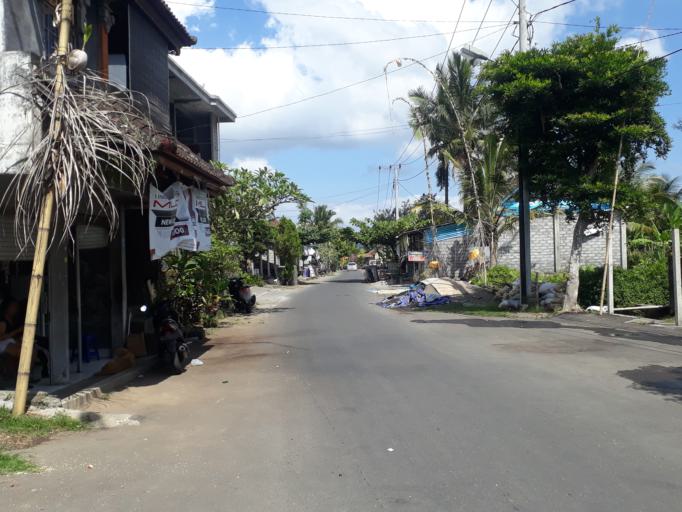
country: ID
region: Bali
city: Banjar Wangsian
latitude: -8.4717
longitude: 115.4443
